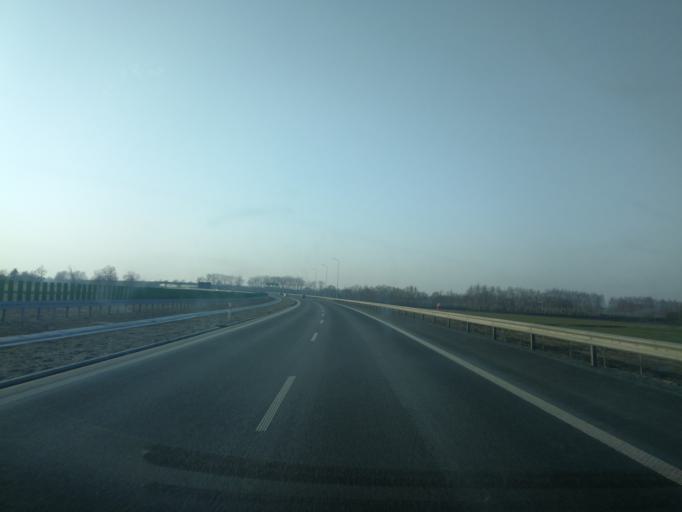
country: PL
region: Warmian-Masurian Voivodeship
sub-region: Powiat elblaski
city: Elblag
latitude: 54.1612
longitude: 19.3566
